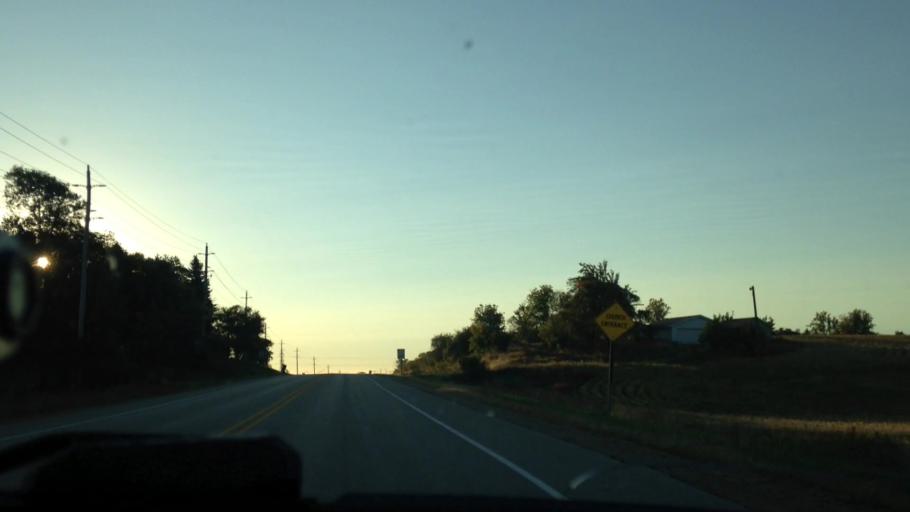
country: US
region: Wisconsin
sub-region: Ozaukee County
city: Saukville
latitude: 43.3893
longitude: -87.9669
